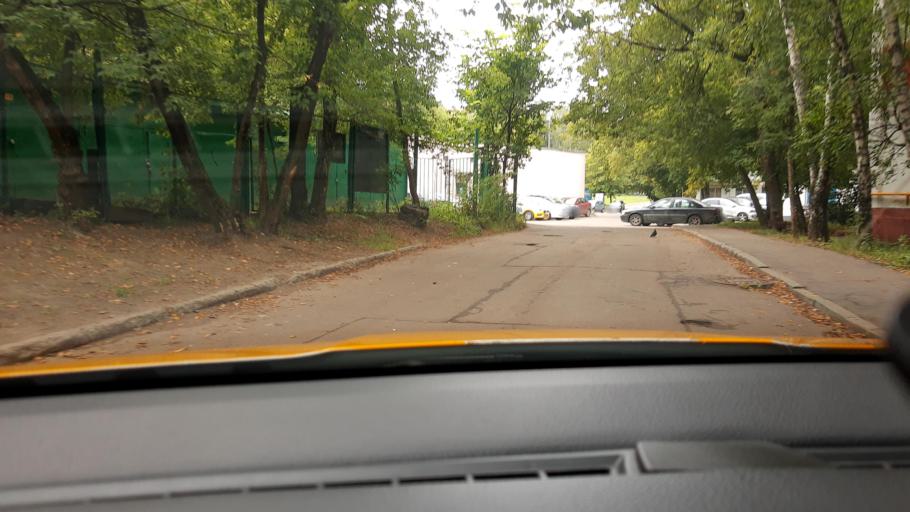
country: RU
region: Moscow
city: Gol'yanovo
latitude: 55.8181
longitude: 37.8045
